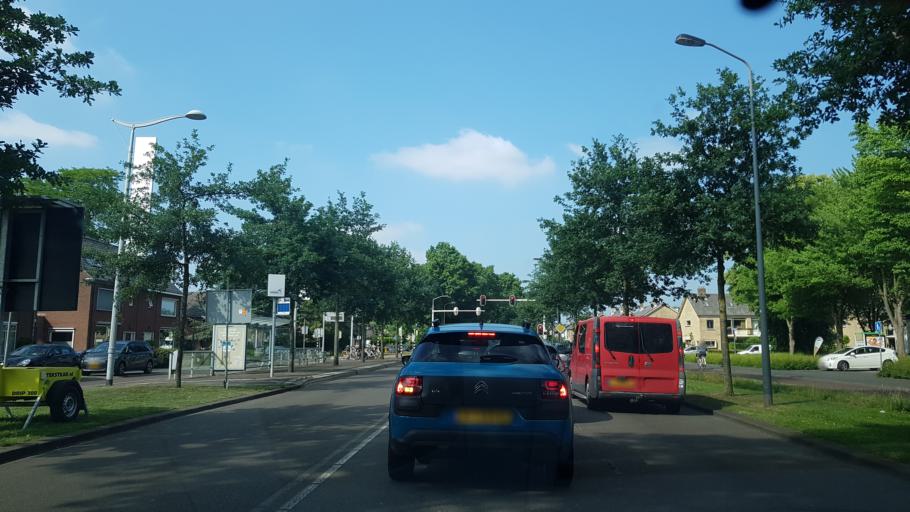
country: NL
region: North Brabant
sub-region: Gemeente Breda
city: Hoge Vucht
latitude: 51.6095
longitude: 4.8213
